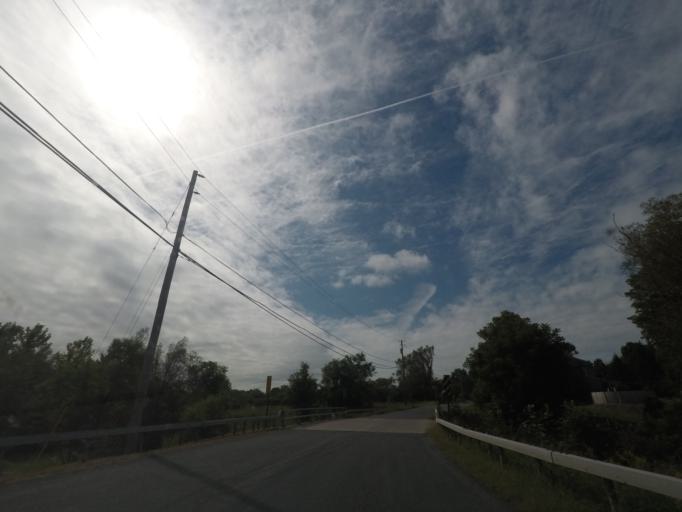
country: US
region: New York
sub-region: Rensselaer County
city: Nassau
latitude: 42.5633
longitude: -73.6273
